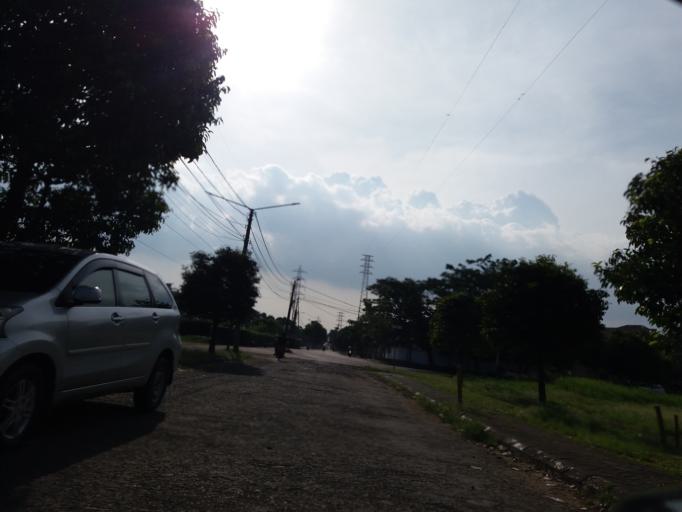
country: ID
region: West Java
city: Bandung
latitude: -6.9622
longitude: 107.6261
